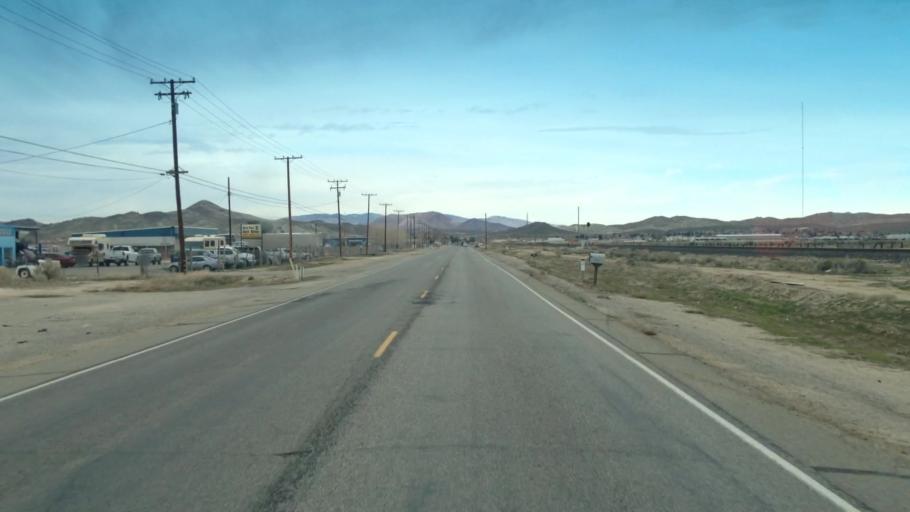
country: US
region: California
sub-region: Kern County
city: Rosamond
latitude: 34.8414
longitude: -118.1594
